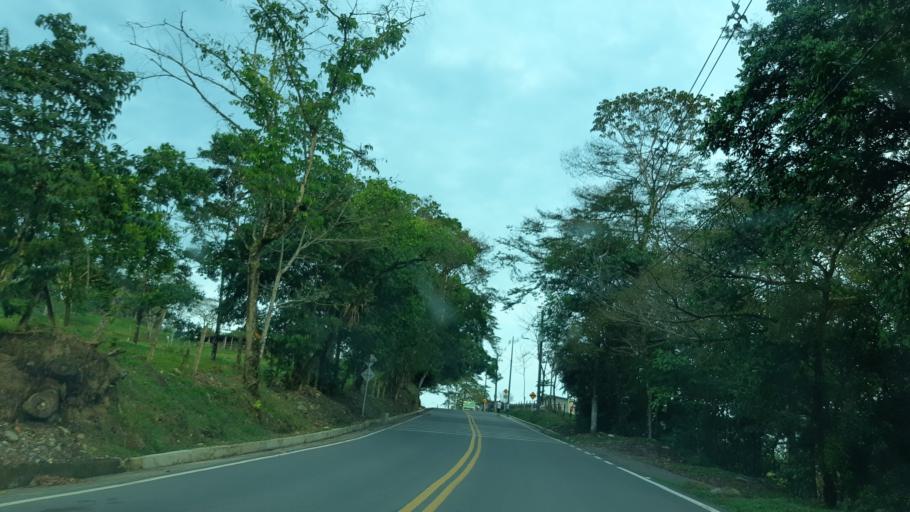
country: CO
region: Casanare
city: Sabanalarga
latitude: 4.8190
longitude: -73.0718
